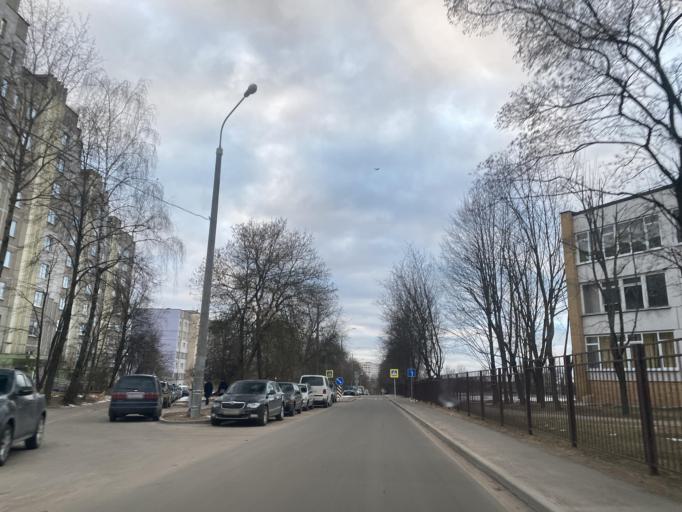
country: BY
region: Minsk
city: Borovlyany
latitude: 53.9565
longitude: 27.6312
